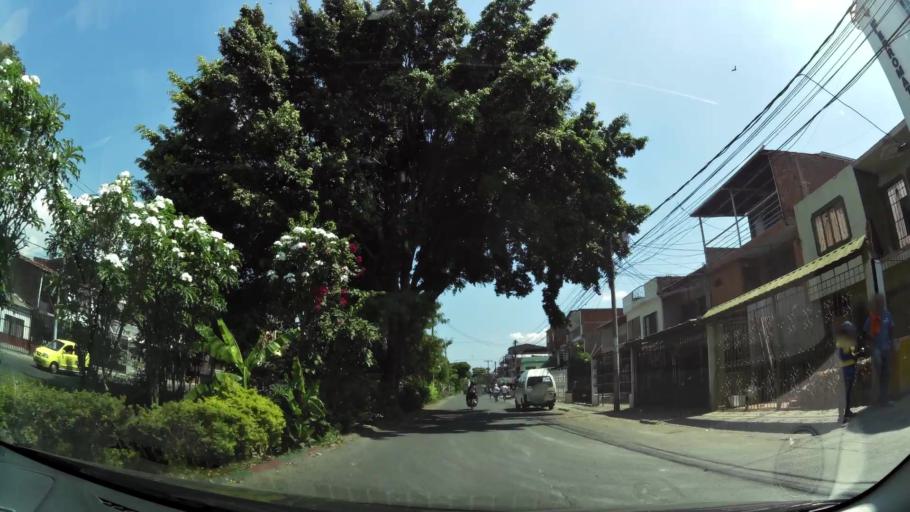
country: CO
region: Valle del Cauca
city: Cali
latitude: 3.4284
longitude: -76.5040
